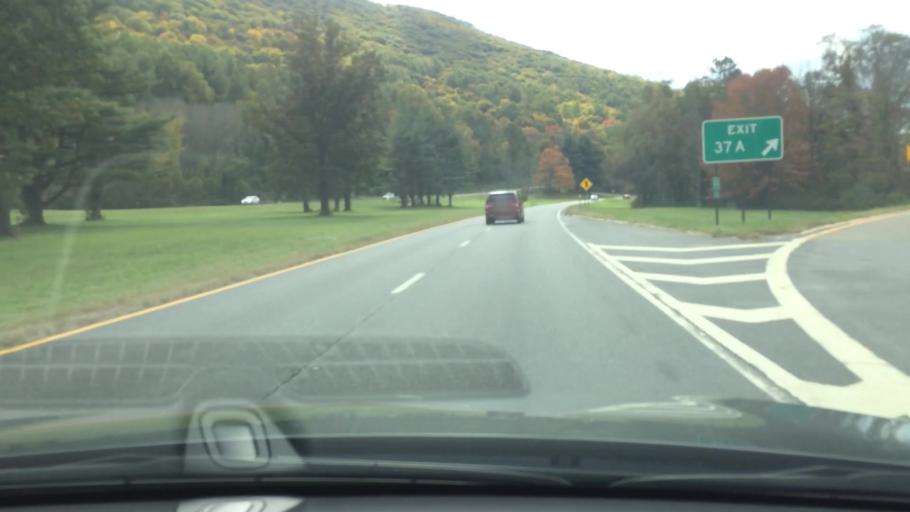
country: US
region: New York
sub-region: Dutchess County
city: Hillside Lake
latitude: 41.5376
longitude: -73.7717
